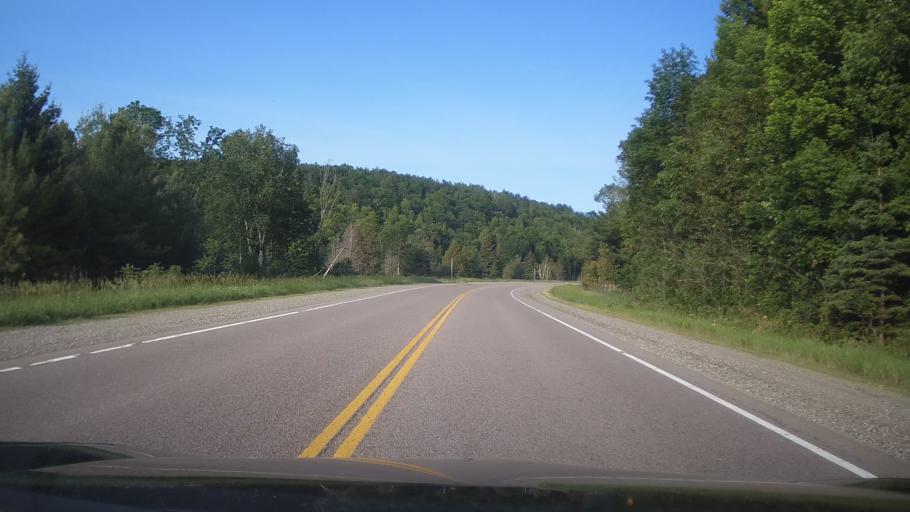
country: CA
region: Ontario
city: Skatepark
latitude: 44.7585
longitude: -76.7733
